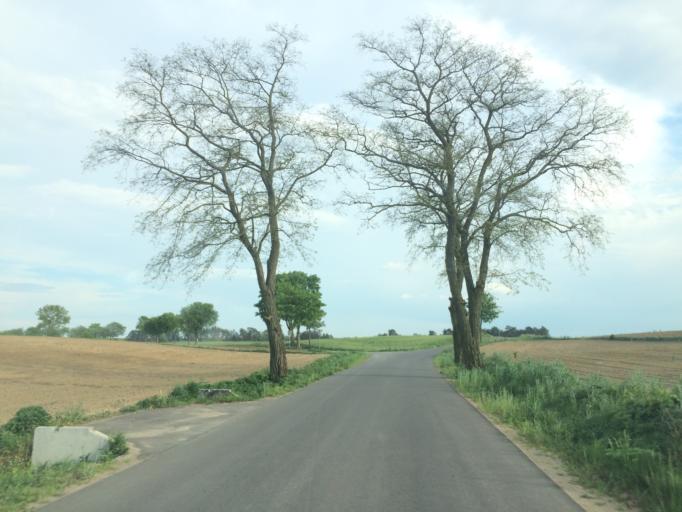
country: PL
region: Kujawsko-Pomorskie
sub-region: Powiat brodnicki
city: Brzozie
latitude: 53.3758
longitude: 19.7103
